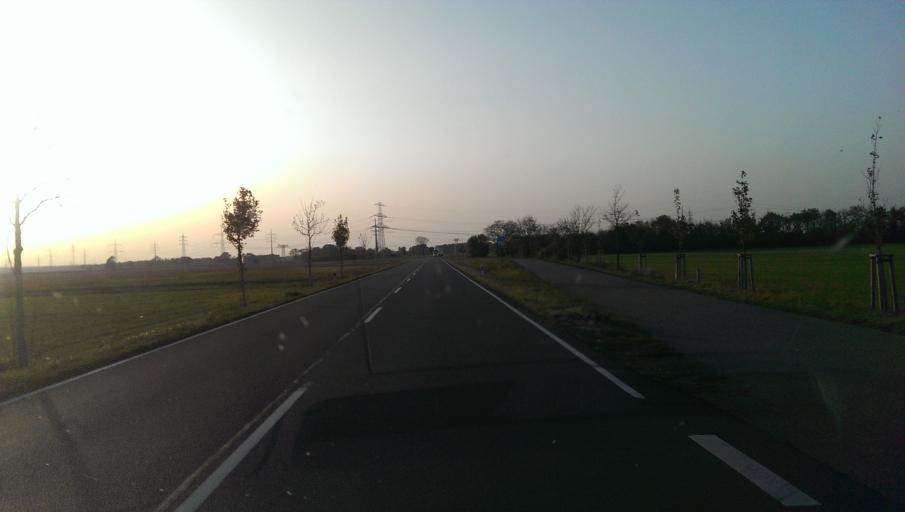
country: DE
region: Saxony-Anhalt
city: Annaburg
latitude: 51.7878
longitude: 13.0586
